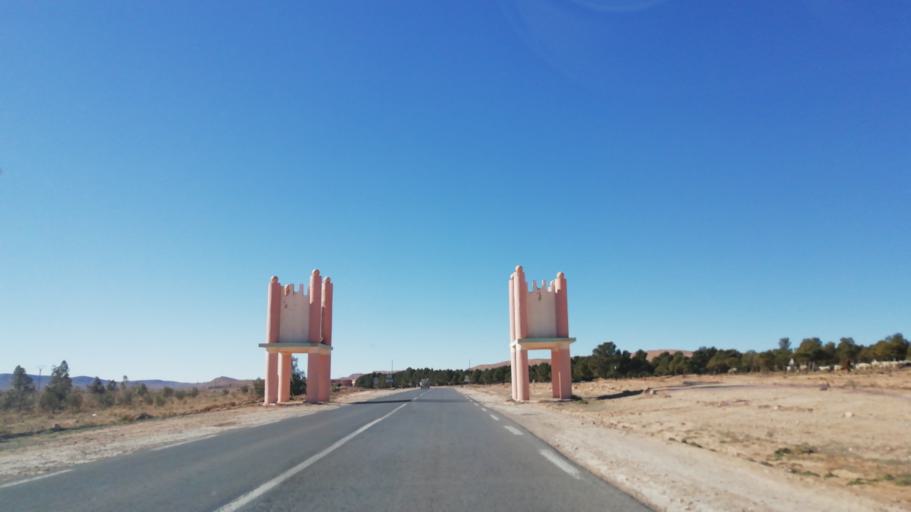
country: DZ
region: El Bayadh
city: El Bayadh
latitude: 33.7225
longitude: 1.5209
